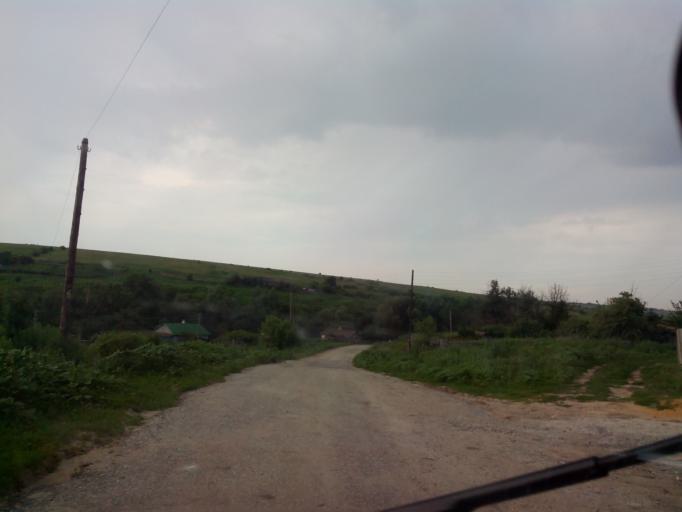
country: RU
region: Volgograd
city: Slashchevskaya
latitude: 49.7777
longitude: 42.4577
